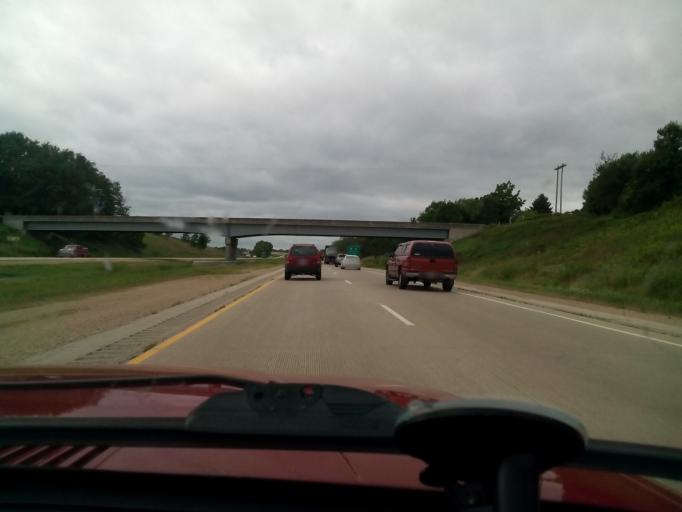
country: US
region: Wisconsin
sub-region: Columbia County
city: Columbus
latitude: 43.3565
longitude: -89.0077
